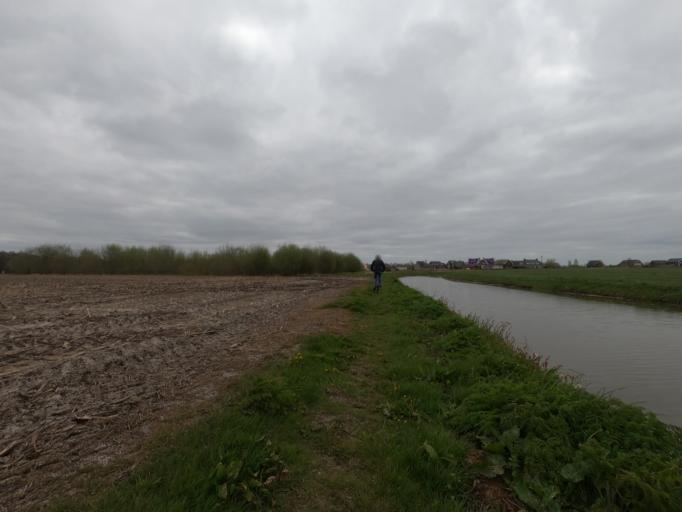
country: NL
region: Drenthe
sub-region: Gemeente Coevorden
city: Sleen
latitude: 52.7582
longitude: 6.8457
